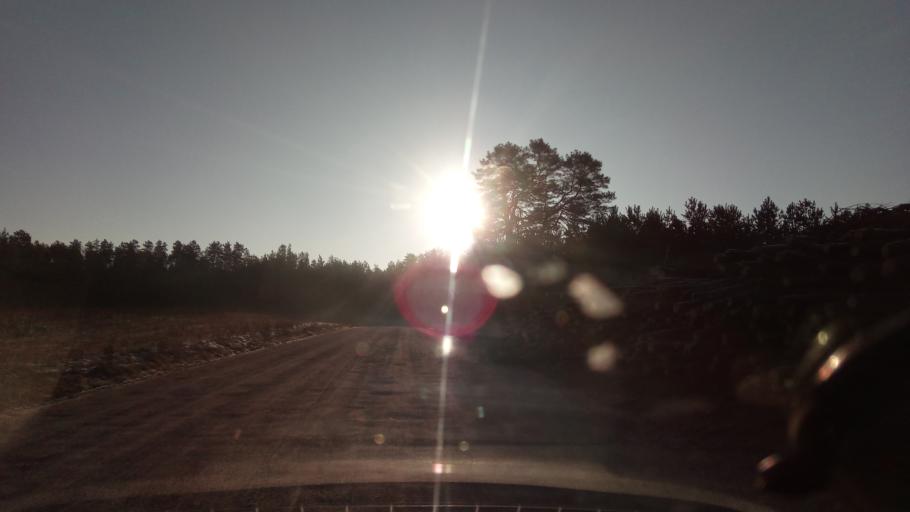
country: LT
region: Alytaus apskritis
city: Druskininkai
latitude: 54.1491
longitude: 23.9357
